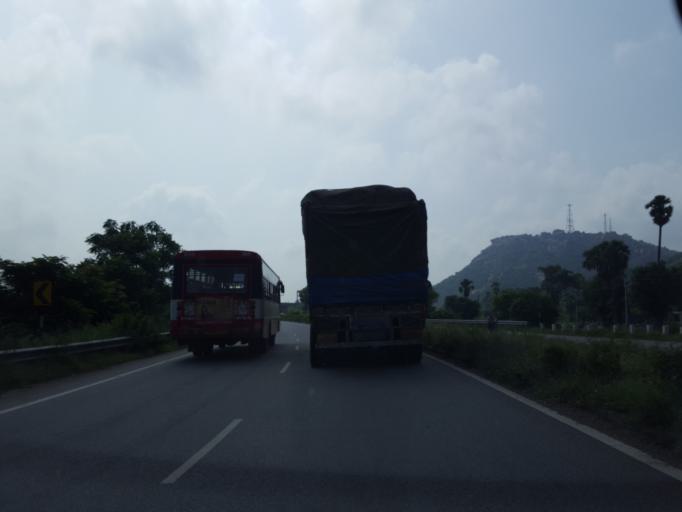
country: IN
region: Telangana
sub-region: Rangareddi
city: Ghatkesar
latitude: 17.2960
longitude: 78.7409
